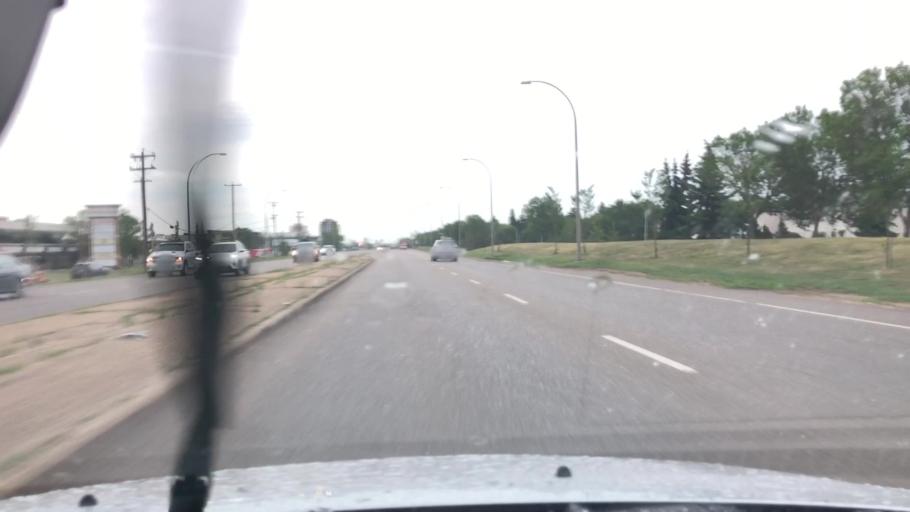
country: CA
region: Alberta
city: St. Albert
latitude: 53.5470
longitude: -113.6124
